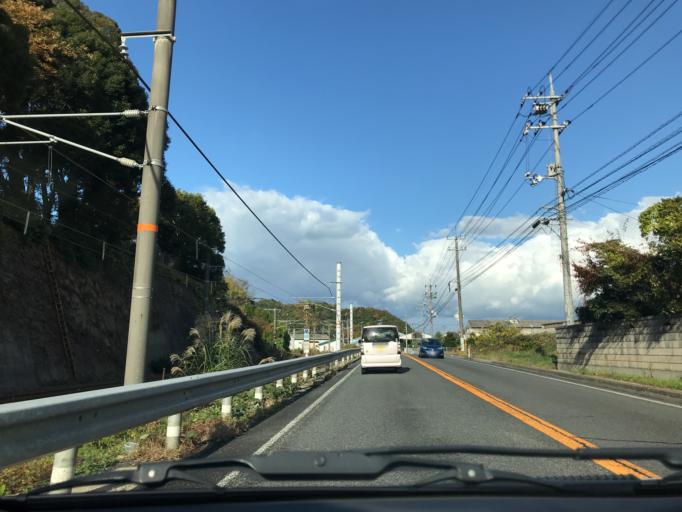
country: JP
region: Shimane
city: Yasugicho
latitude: 35.4261
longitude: 133.2755
